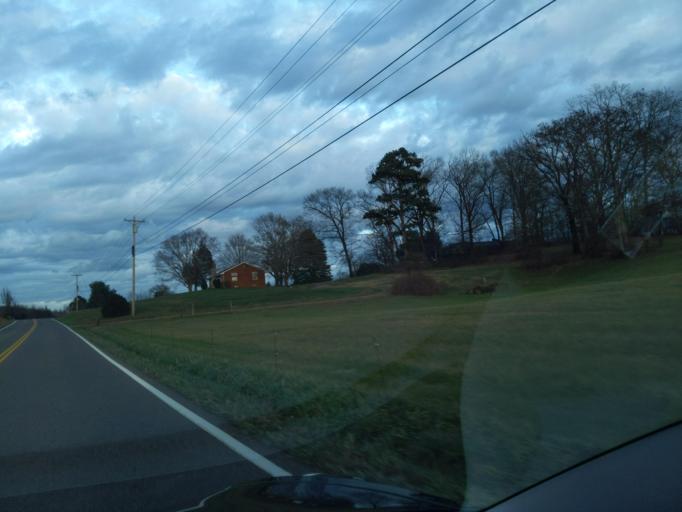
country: US
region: Tennessee
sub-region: Jefferson County
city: Dandridge
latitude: 35.9942
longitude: -83.4510
